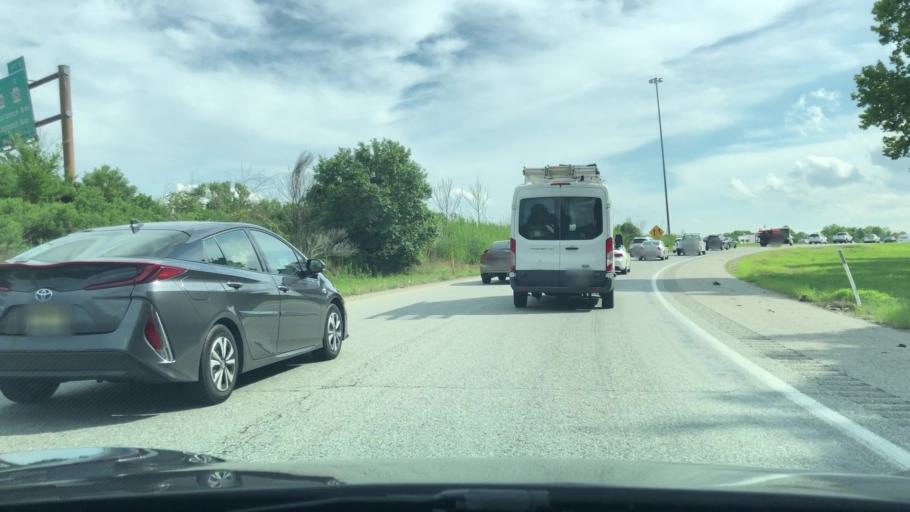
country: US
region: Pennsylvania
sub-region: Delaware County
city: Eddystone
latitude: 39.8671
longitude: -75.3455
